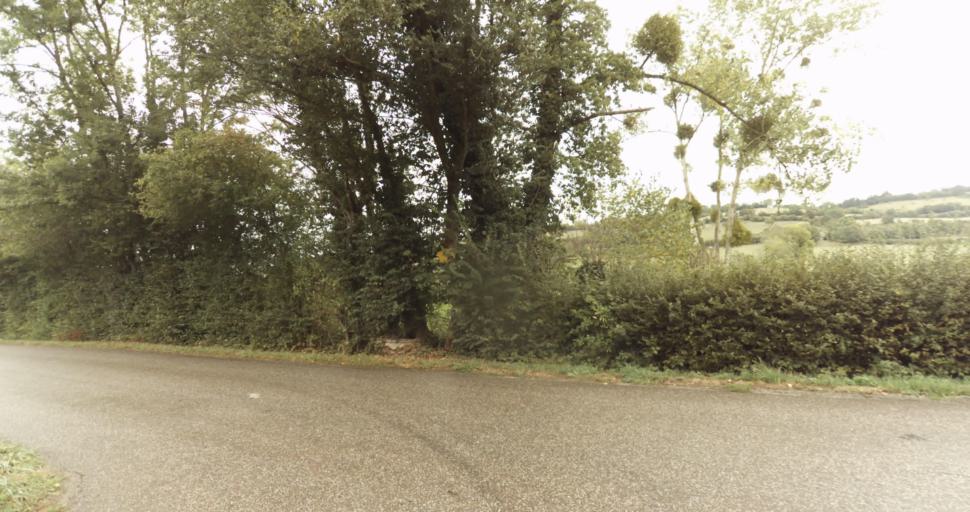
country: FR
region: Lower Normandy
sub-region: Departement de l'Orne
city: Vimoutiers
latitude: 48.8803
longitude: 0.2178
